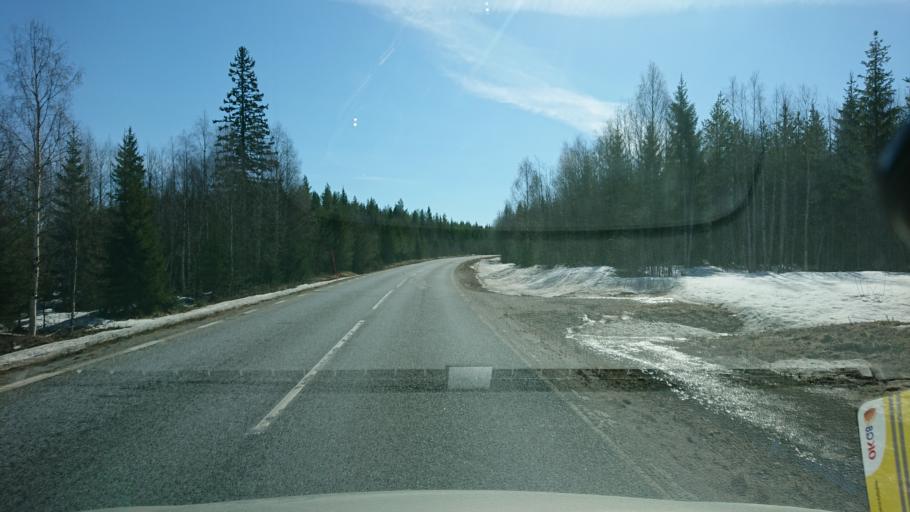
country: SE
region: Vaesterbotten
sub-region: Dorotea Kommun
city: Dorotea
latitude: 63.9948
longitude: 16.3120
